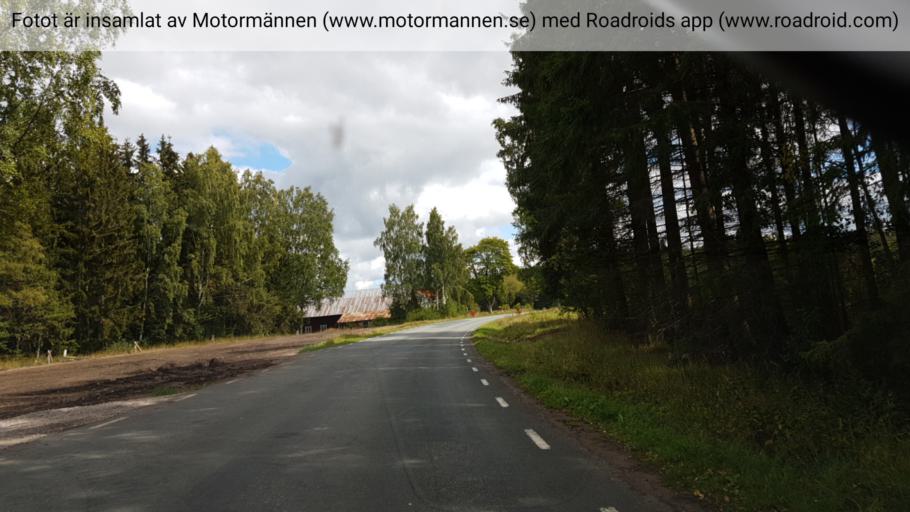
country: SE
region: Joenkoeping
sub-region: Aneby Kommun
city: Aneby
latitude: 57.8223
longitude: 14.8665
